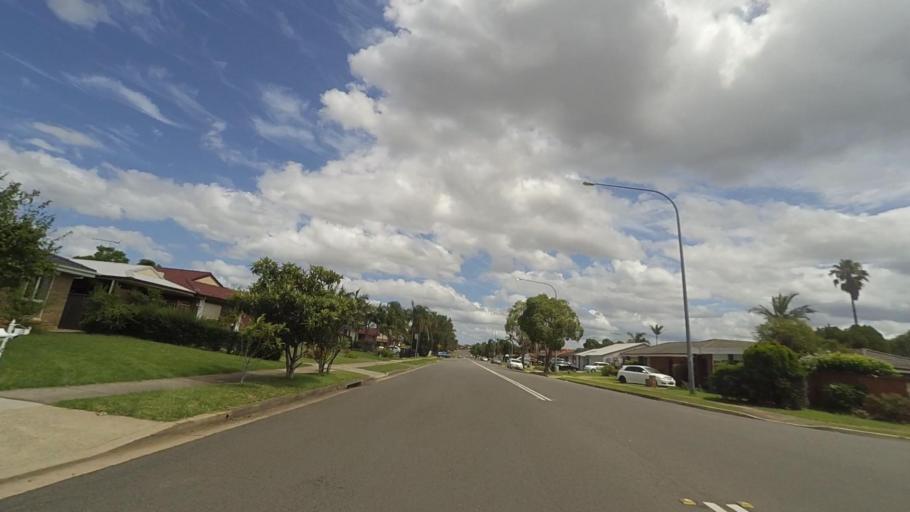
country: AU
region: New South Wales
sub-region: Fairfield
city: Fairfield Heights
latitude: -33.8686
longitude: 150.9113
